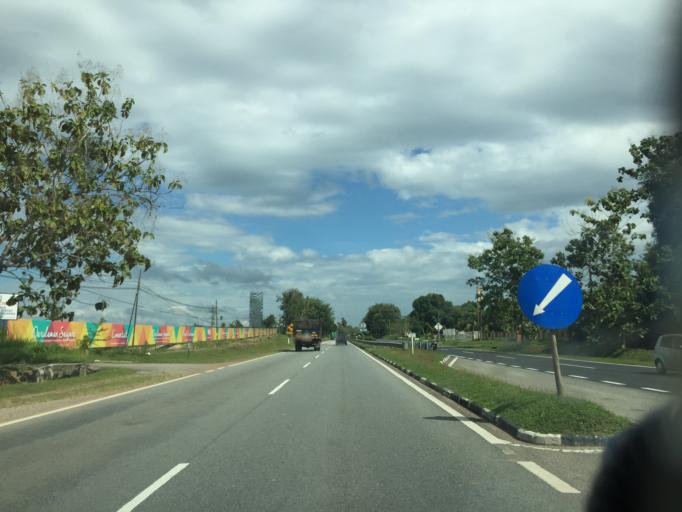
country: MY
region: Kedah
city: Jitra
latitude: 6.3362
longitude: 100.4204
